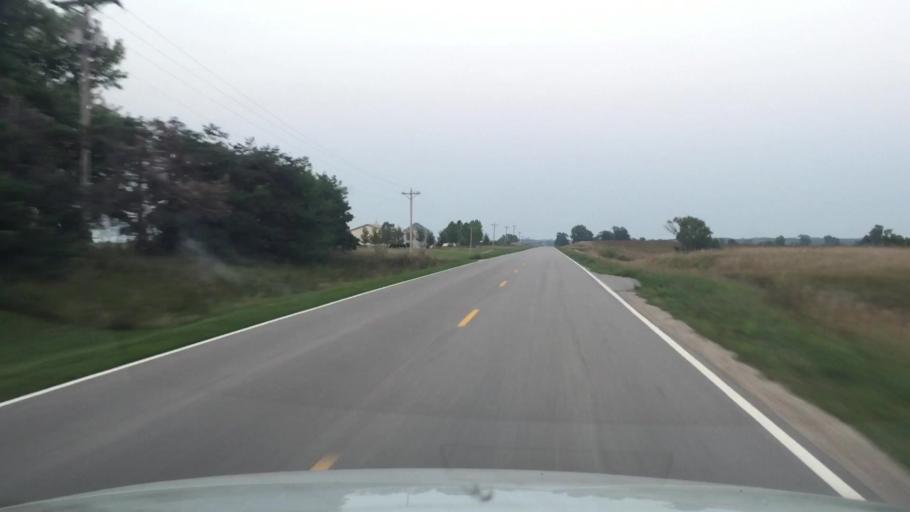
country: US
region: Iowa
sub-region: Warren County
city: Indianola
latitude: 41.1907
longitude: -93.5769
